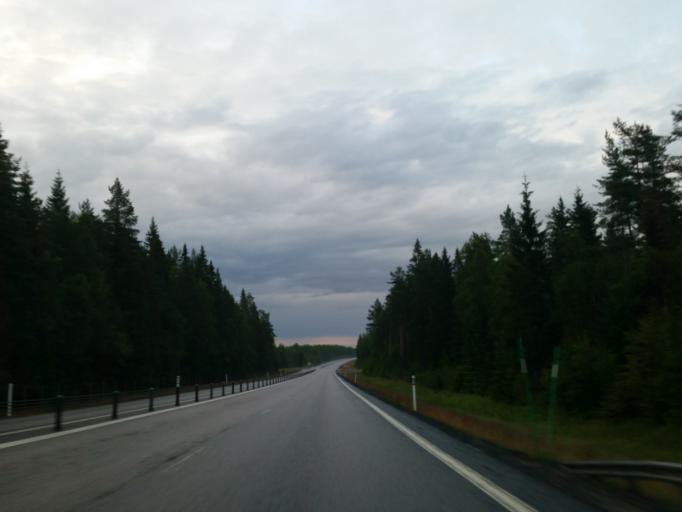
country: SE
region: Vaesterbotten
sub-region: Umea Kommun
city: Saevar
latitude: 63.9795
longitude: 20.7251
